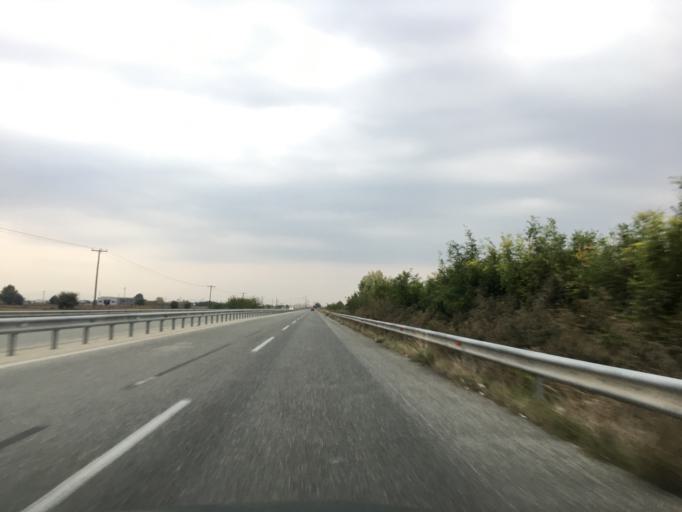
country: GR
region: Thessaly
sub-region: Trikala
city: Megalochori
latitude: 39.5650
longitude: 21.8495
